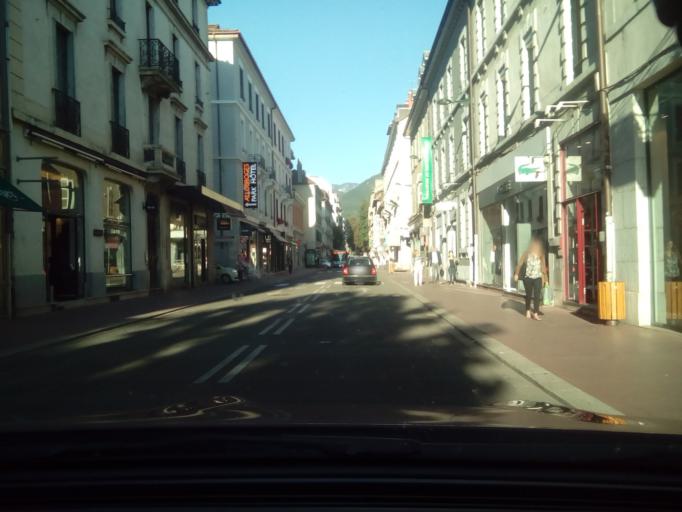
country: FR
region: Rhone-Alpes
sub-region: Departement de la Haute-Savoie
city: Annecy
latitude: 45.9018
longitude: 6.1234
